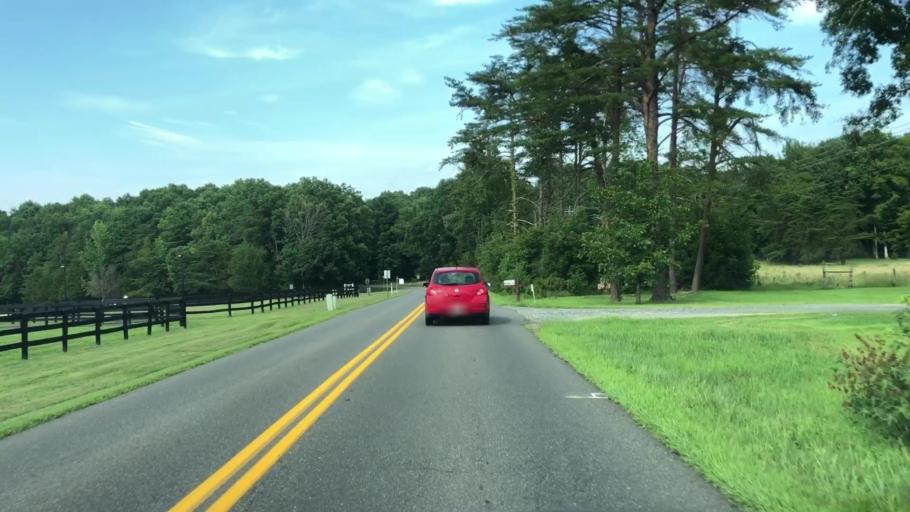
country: US
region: Virginia
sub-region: Stafford County
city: Falmouth
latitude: 38.4055
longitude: -77.5139
